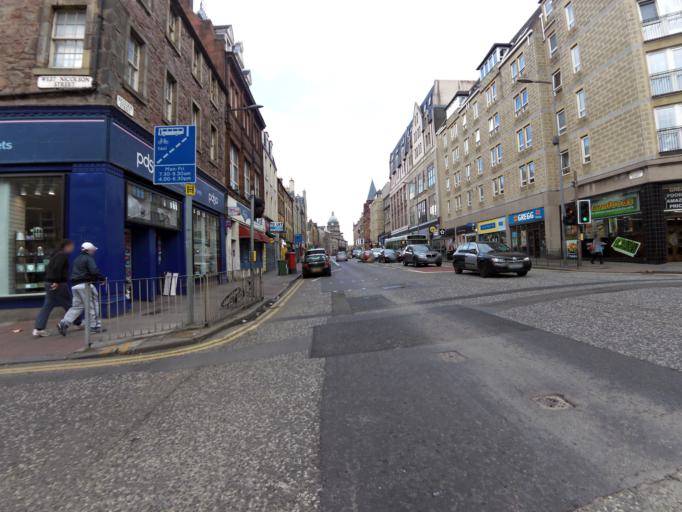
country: GB
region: Scotland
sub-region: Edinburgh
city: Edinburgh
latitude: 55.9451
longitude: -3.1843
